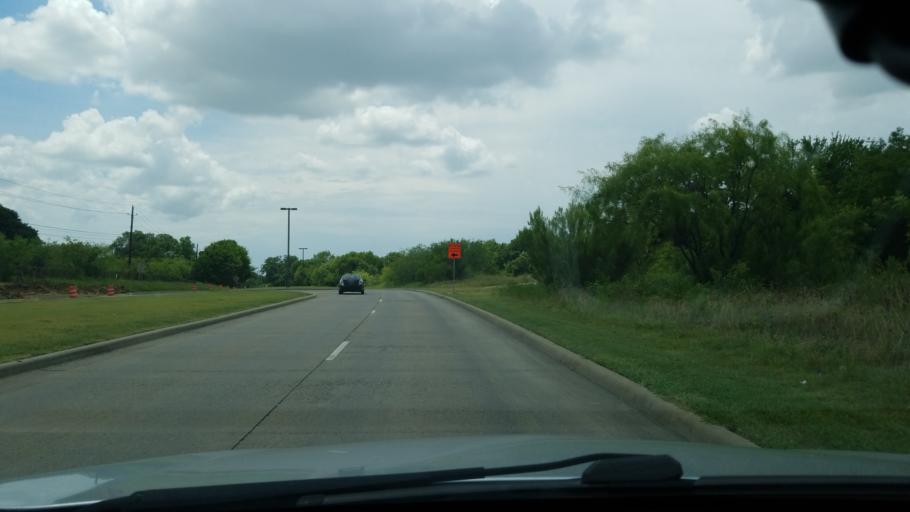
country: US
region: Texas
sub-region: Dallas County
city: Coppell
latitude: 32.9553
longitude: -96.9718
